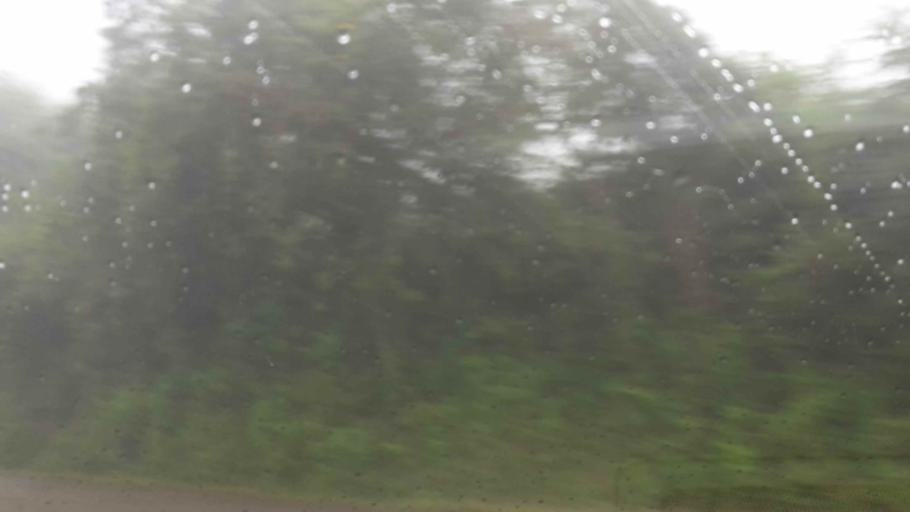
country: BO
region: Cochabamba
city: Colomi
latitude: -17.0904
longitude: -65.9966
